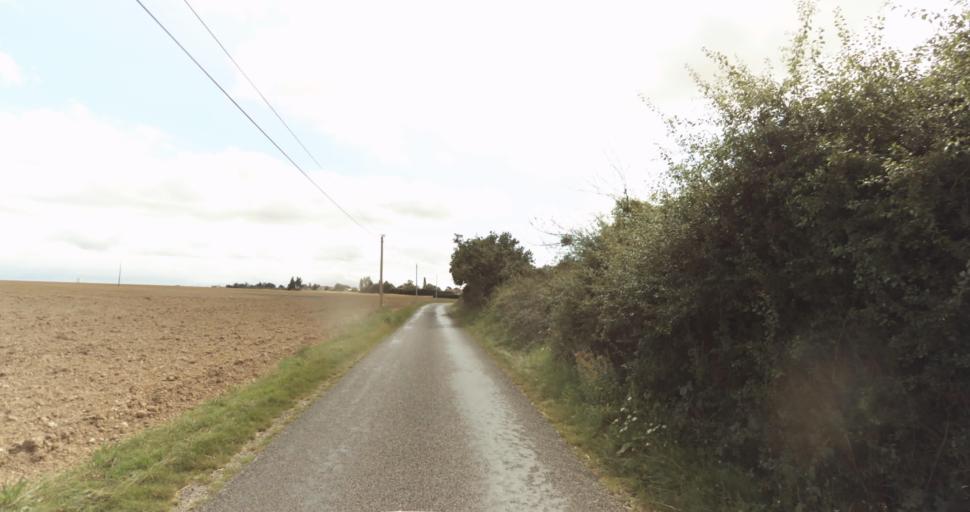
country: FR
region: Haute-Normandie
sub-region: Departement de l'Eure
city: Evreux
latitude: 48.9280
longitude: 1.2498
